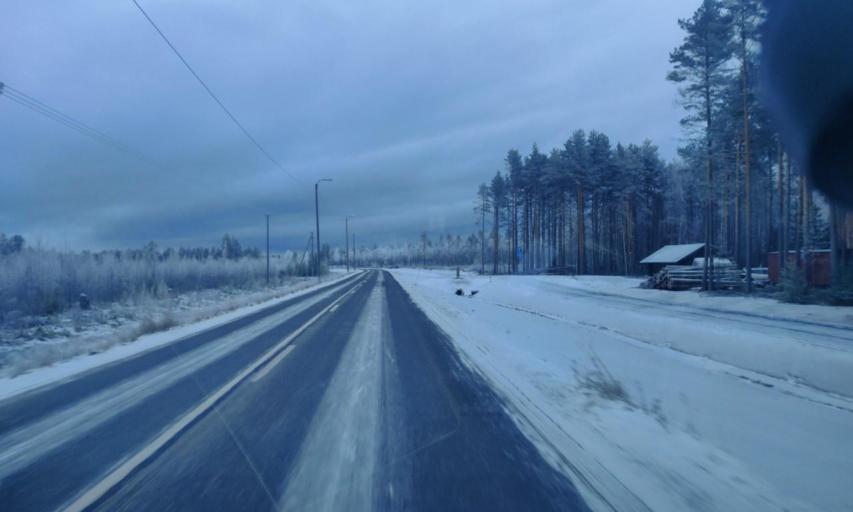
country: FI
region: Northern Ostrobothnia
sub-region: Oulu
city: Oulunsalo
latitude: 64.9899
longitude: 25.2577
